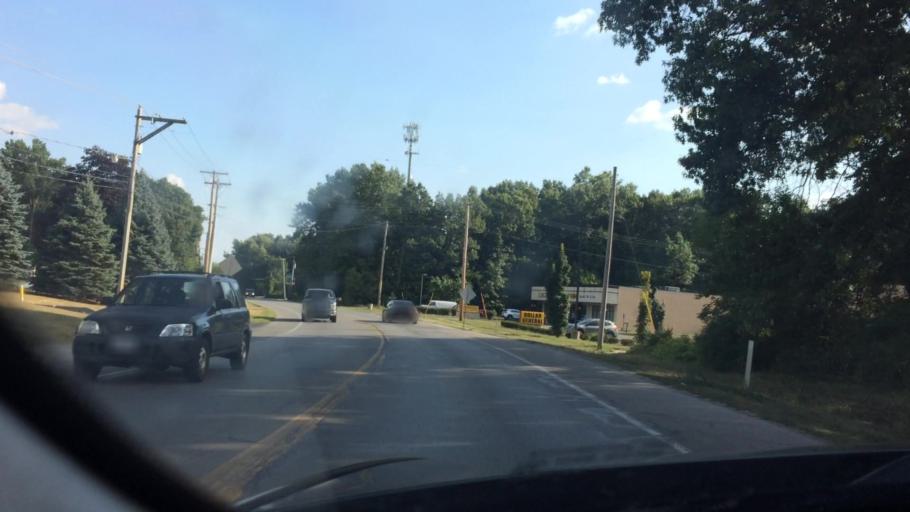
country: US
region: Ohio
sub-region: Lucas County
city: Holland
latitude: 41.6528
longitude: -83.7035
